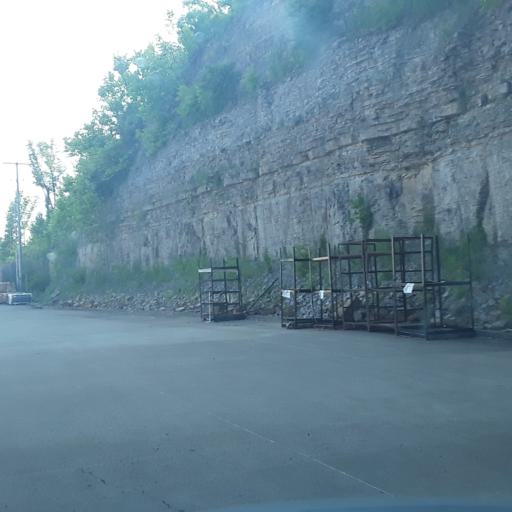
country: US
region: Tennessee
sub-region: Williamson County
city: Brentwood Estates
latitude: 36.0409
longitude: -86.7085
